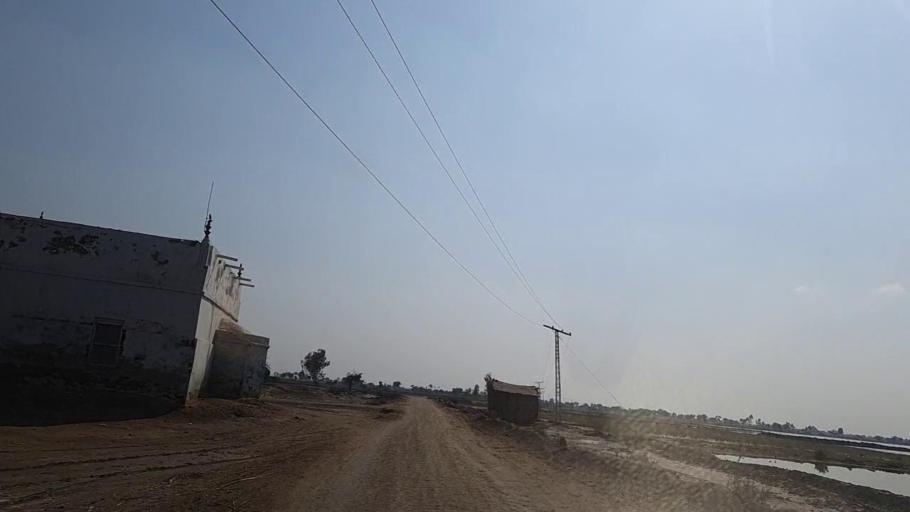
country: PK
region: Sindh
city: Daur
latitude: 26.4595
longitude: 68.2505
